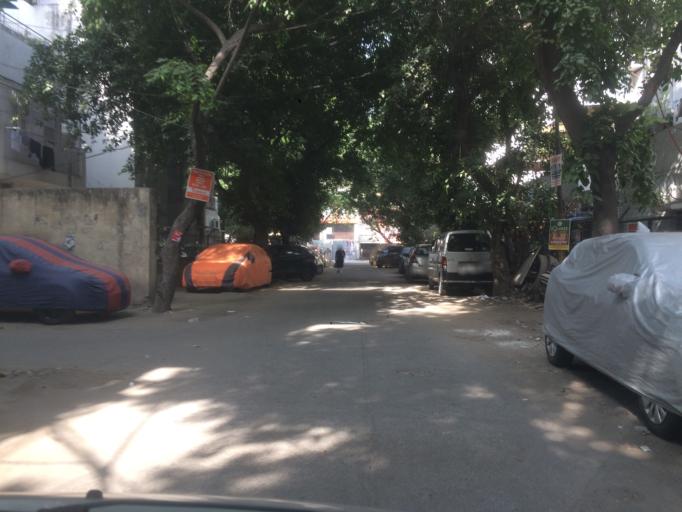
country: IN
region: Uttar Pradesh
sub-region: Gautam Buddha Nagar
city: Noida
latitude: 28.5431
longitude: 77.2472
